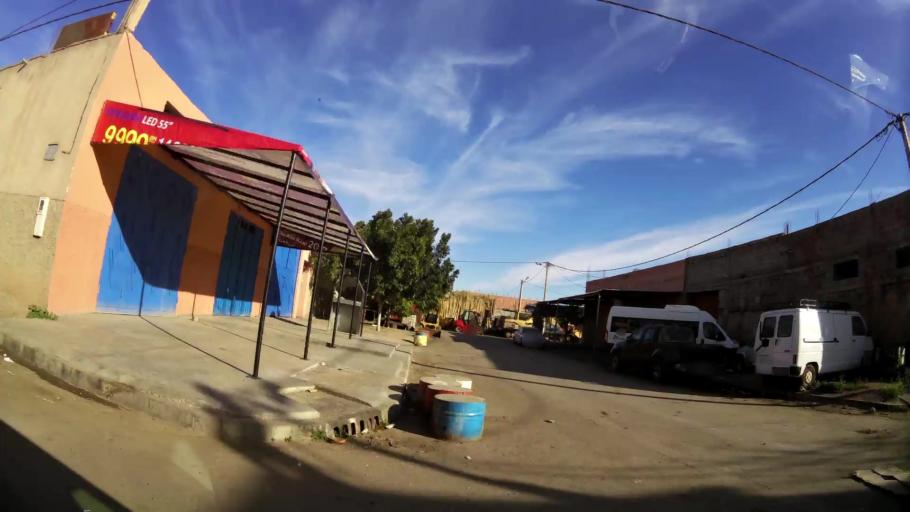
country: MA
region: Marrakech-Tensift-Al Haouz
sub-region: Marrakech
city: Marrakesh
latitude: 31.6856
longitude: -8.0562
